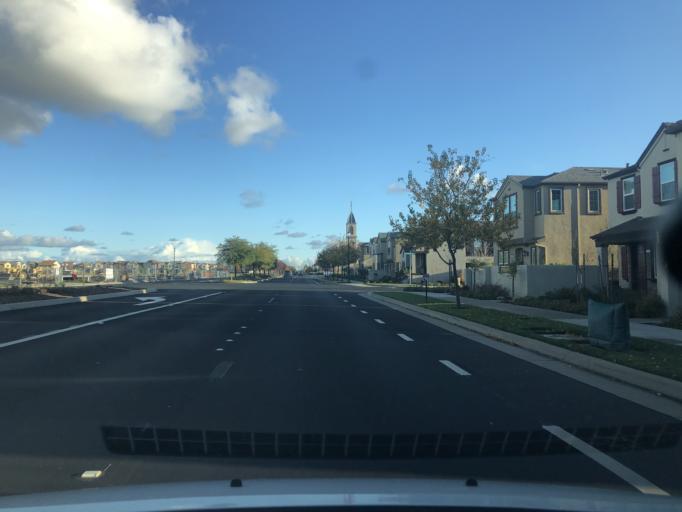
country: US
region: California
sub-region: Sacramento County
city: Antelope
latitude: 38.7730
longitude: -121.3716
